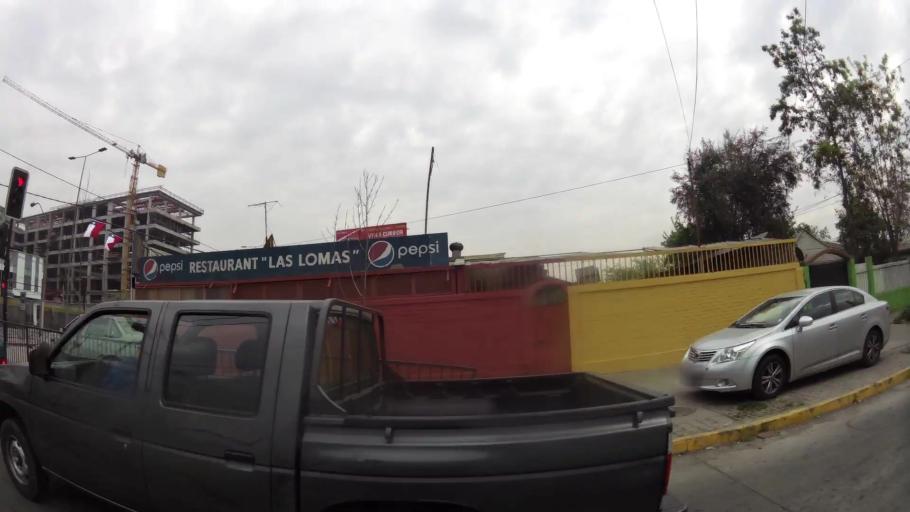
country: CL
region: Santiago Metropolitan
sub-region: Provincia de Santiago
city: Villa Presidente Frei, Nunoa, Santiago, Chile
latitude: -33.5091
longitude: -70.5974
